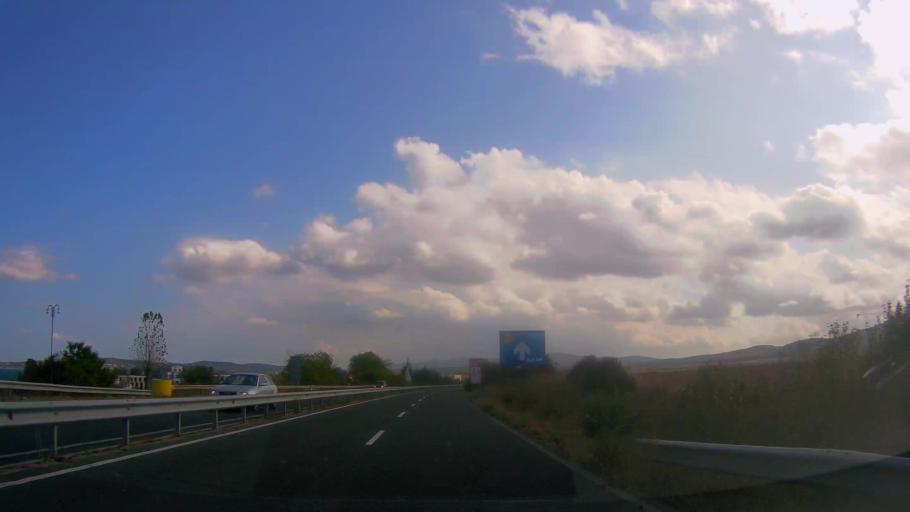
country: BG
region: Burgas
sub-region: Obshtina Sozopol
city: Chernomorets
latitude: 42.4306
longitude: 27.6392
